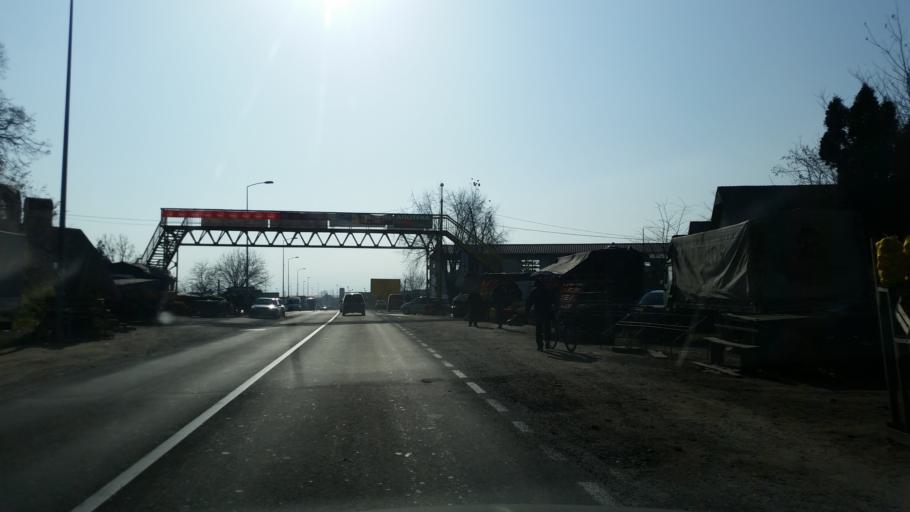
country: RS
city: Prislonica
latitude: 43.9163
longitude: 20.4076
